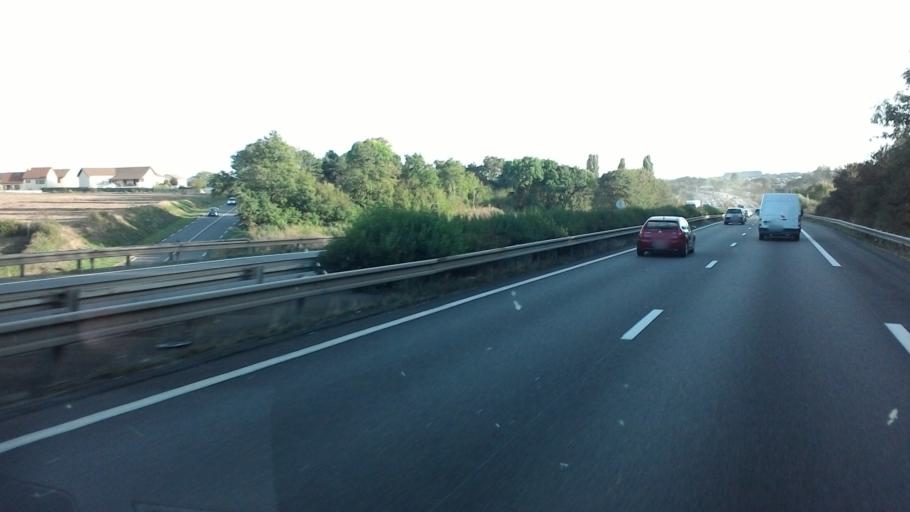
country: FR
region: Lorraine
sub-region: Departement de la Moselle
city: Bertrange
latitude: 49.3183
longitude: 6.1827
